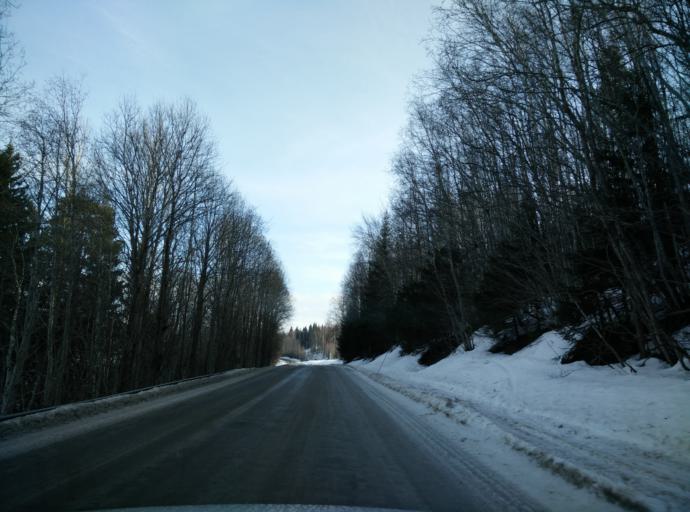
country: SE
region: Vaesternorrland
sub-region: Sundsvalls Kommun
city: Njurundabommen
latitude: 62.2215
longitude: 17.3356
